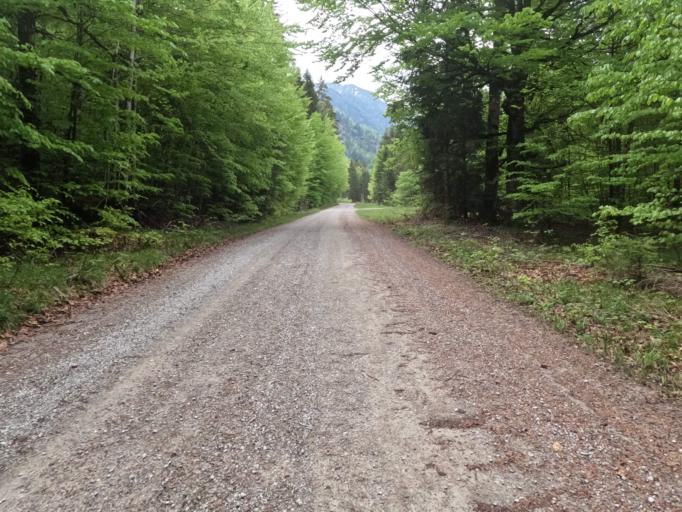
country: DE
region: Bavaria
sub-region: Upper Bavaria
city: Ruhpolding
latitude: 47.7117
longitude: 12.6595
